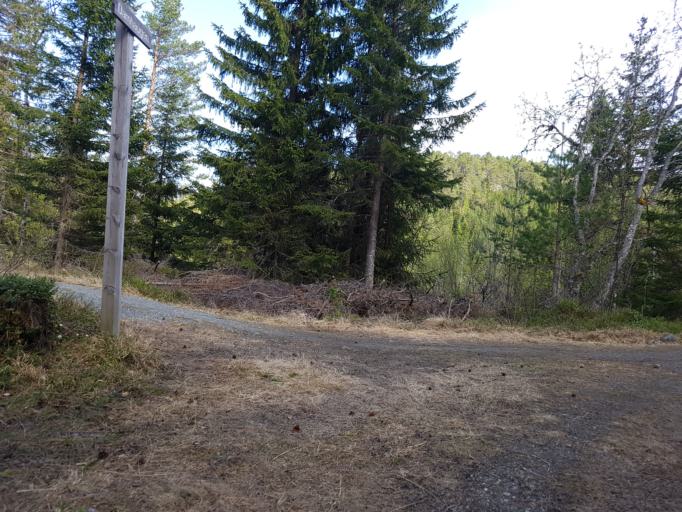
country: NO
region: Sor-Trondelag
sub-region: Trondheim
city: Trondheim
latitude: 63.4419
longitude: 10.2898
